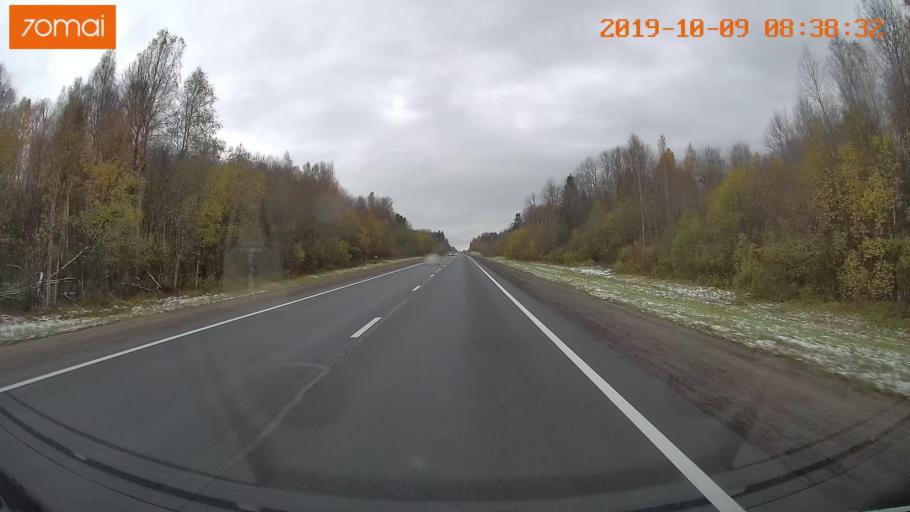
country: RU
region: Vologda
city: Gryazovets
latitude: 58.9578
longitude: 40.1646
